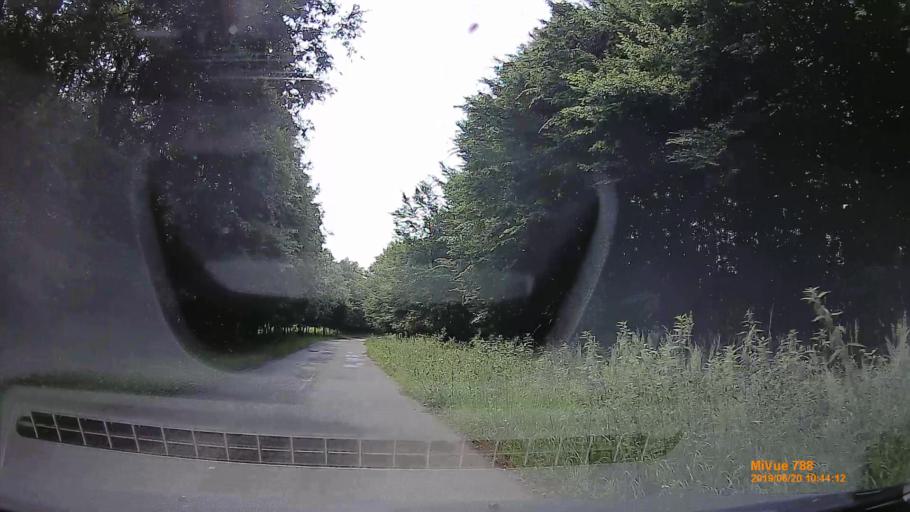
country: HU
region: Baranya
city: Hidas
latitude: 46.1897
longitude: 18.5645
